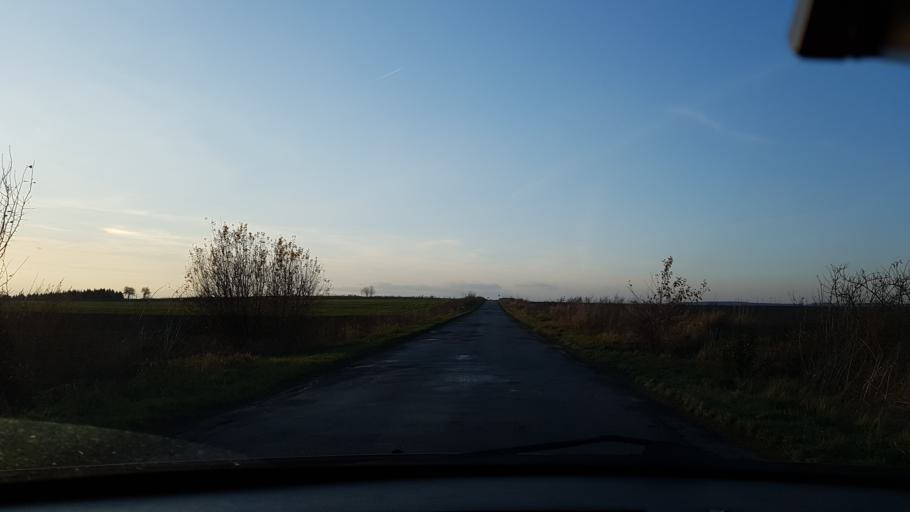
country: PL
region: Lower Silesian Voivodeship
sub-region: Powiat zabkowicki
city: Cieplowody
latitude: 50.6712
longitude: 16.9541
